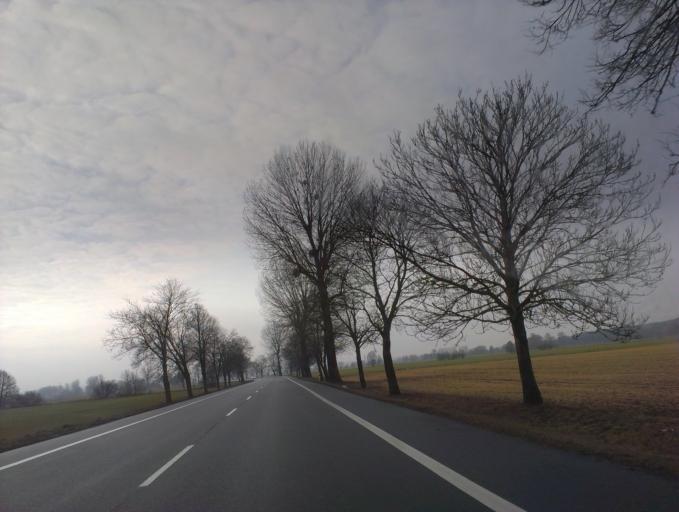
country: PL
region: Greater Poland Voivodeship
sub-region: Powiat pilski
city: Ujscie
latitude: 53.0886
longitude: 16.7348
